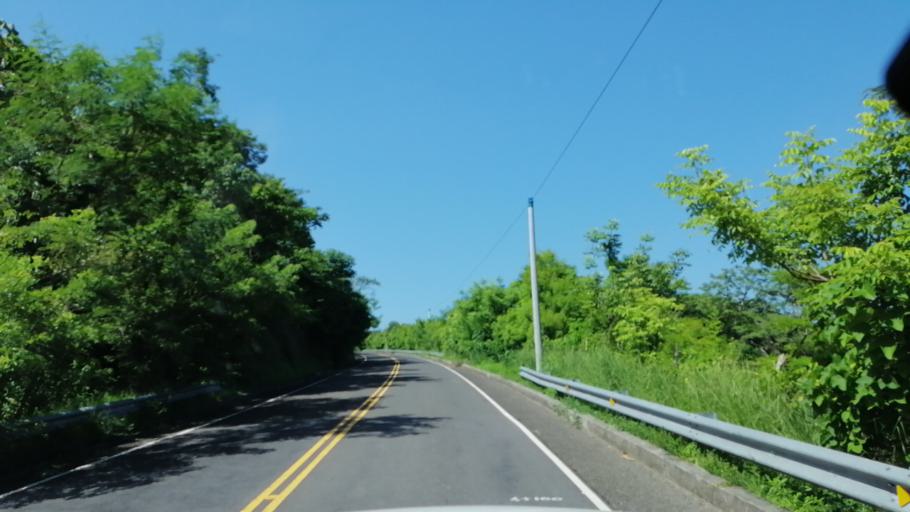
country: HN
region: Lempira
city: La Virtud
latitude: 13.9753
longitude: -88.7636
